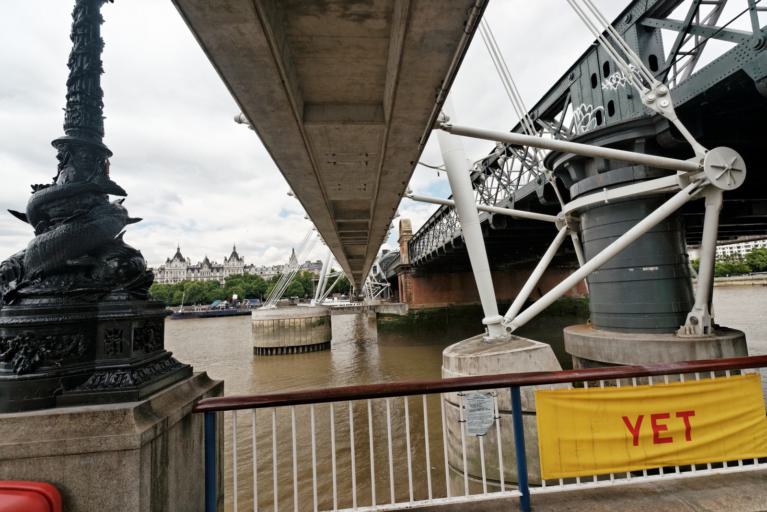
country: GB
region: England
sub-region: Greater London
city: City of Westminster
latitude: 51.5052
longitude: -0.1190
